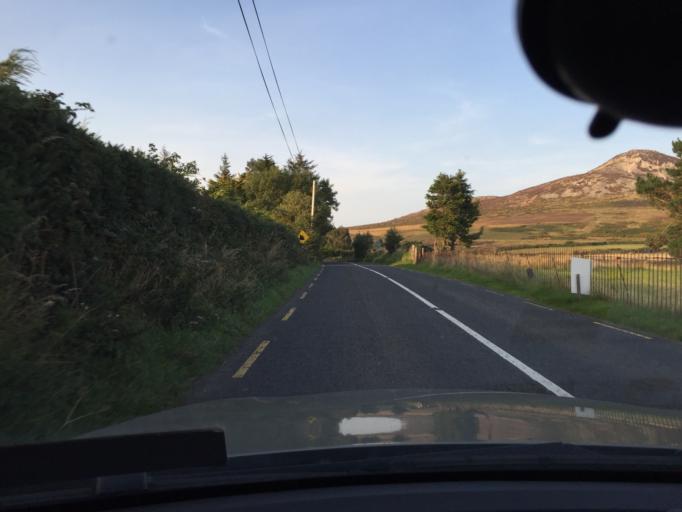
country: IE
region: Leinster
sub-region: Wicklow
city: Kilmacanoge
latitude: 53.1475
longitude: -6.1649
